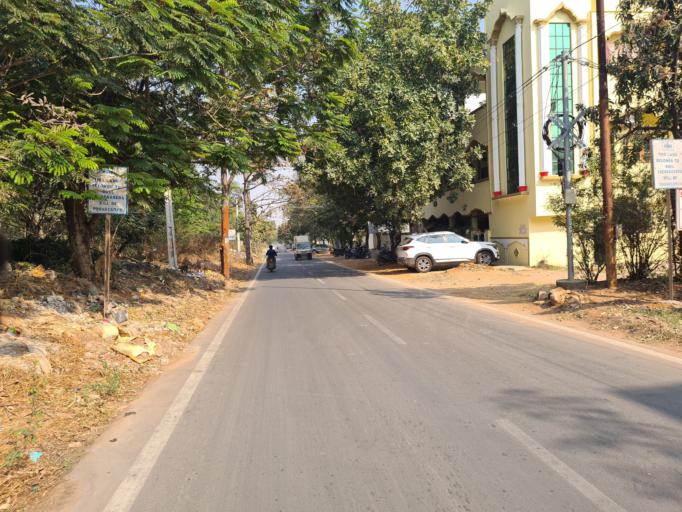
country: IN
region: Telangana
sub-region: Medak
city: Serilingampalle
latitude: 17.4854
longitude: 78.3083
